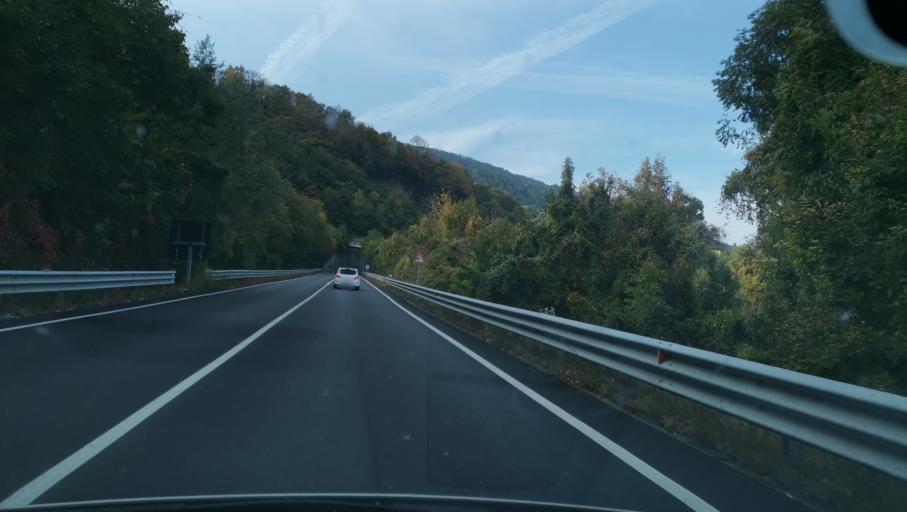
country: IT
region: Piedmont
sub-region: Provincia di Torino
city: Gravere
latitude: 45.1276
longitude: 7.0239
